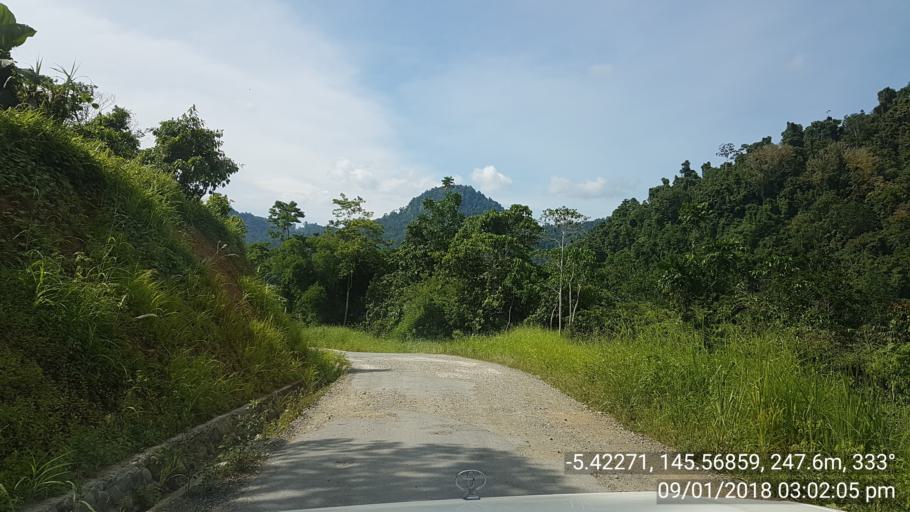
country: PG
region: Madang
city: Madang
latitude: -5.4228
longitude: 145.5686
